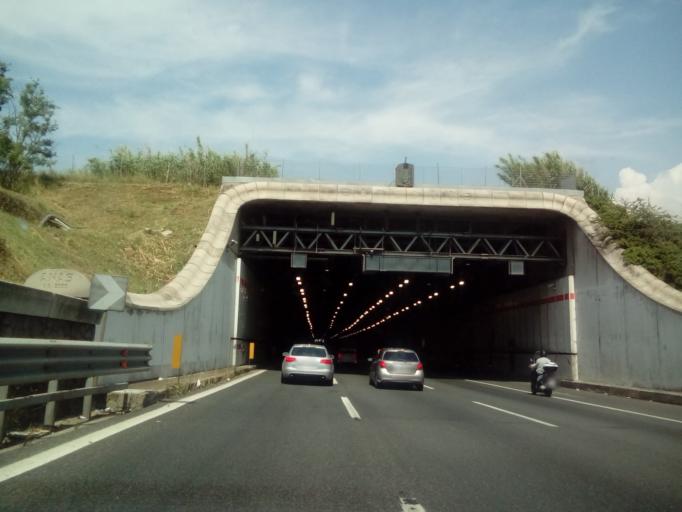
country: IT
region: Latium
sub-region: Citta metropolitana di Roma Capitale
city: Borgo Lotti
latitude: 41.8043
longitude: 12.5587
